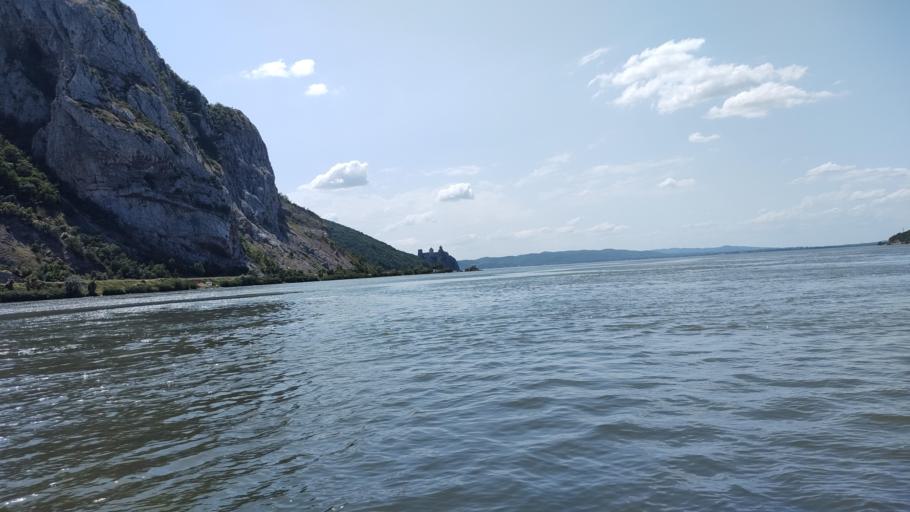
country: RO
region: Caras-Severin
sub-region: Comuna Pescari
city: Coronini
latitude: 44.6623
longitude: 21.7018
